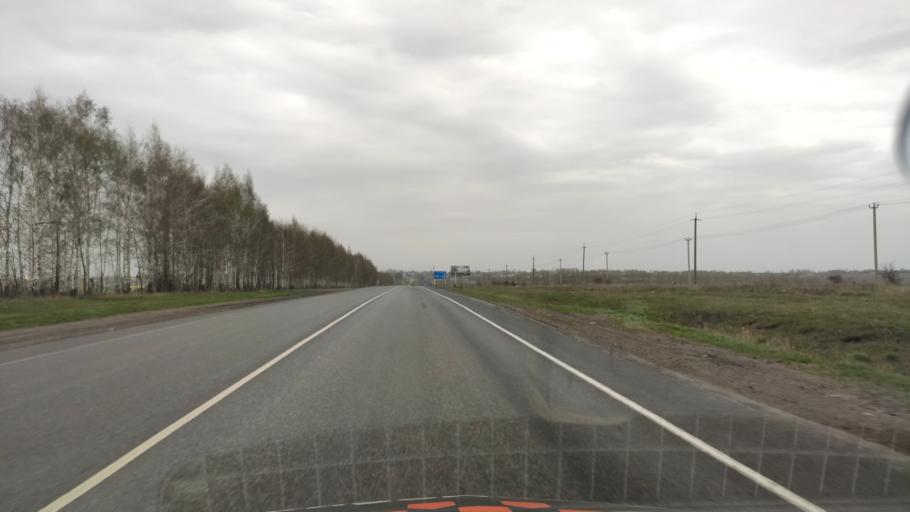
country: RU
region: Kursk
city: Gorshechnoye
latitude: 51.5046
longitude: 37.9914
